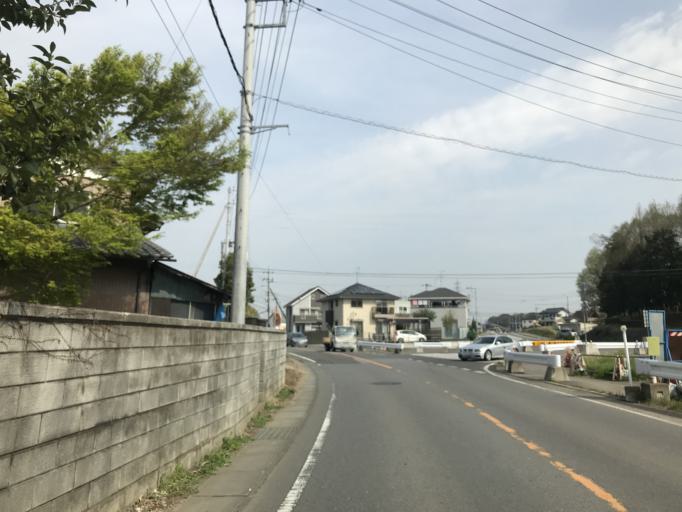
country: JP
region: Ibaraki
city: Moriya
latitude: 35.9687
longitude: 139.9902
